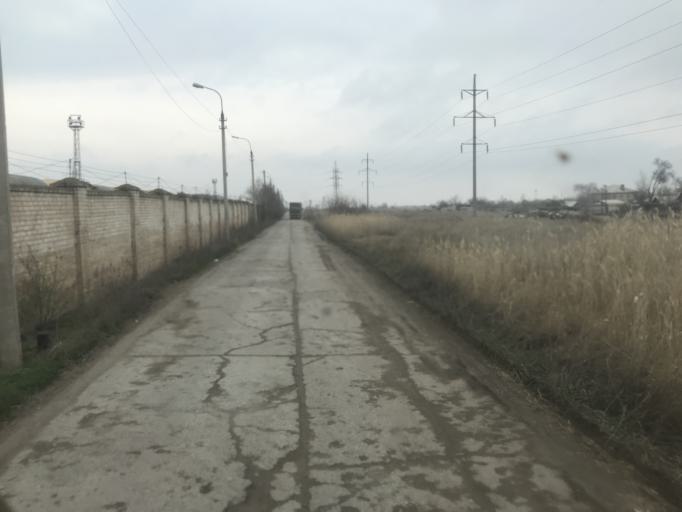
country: RU
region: Volgograd
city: Krasnoslobodsk
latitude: 48.5305
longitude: 44.5884
